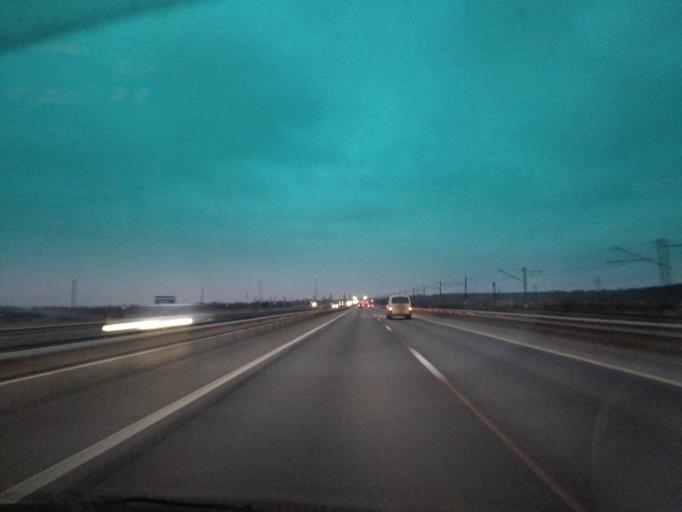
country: RU
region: Adygeya
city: Adygeysk
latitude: 44.8160
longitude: 39.2270
